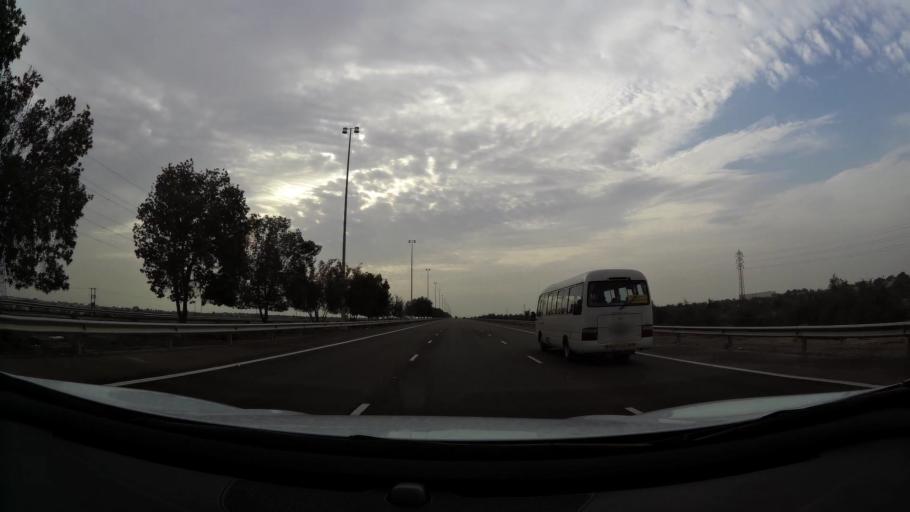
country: AE
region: Abu Dhabi
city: Abu Dhabi
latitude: 24.2119
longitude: 54.8892
